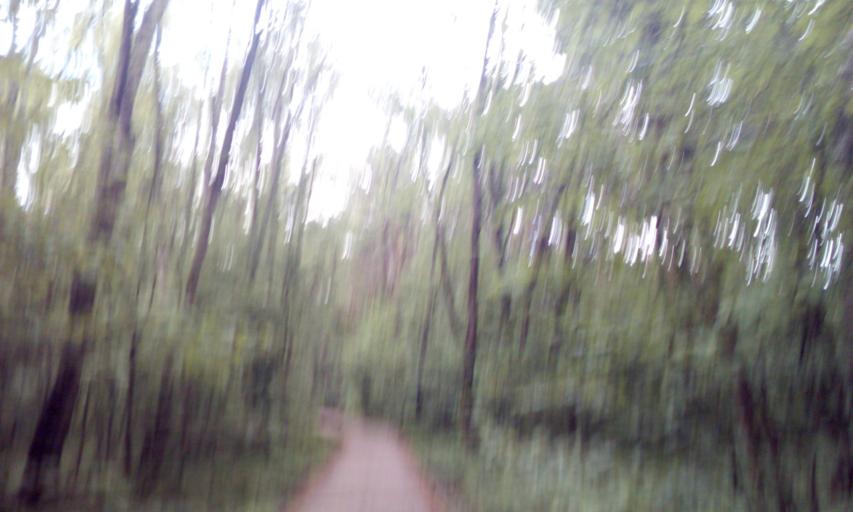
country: RU
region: Moskovskaya
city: Vostryakovo
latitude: 55.6532
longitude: 37.4582
